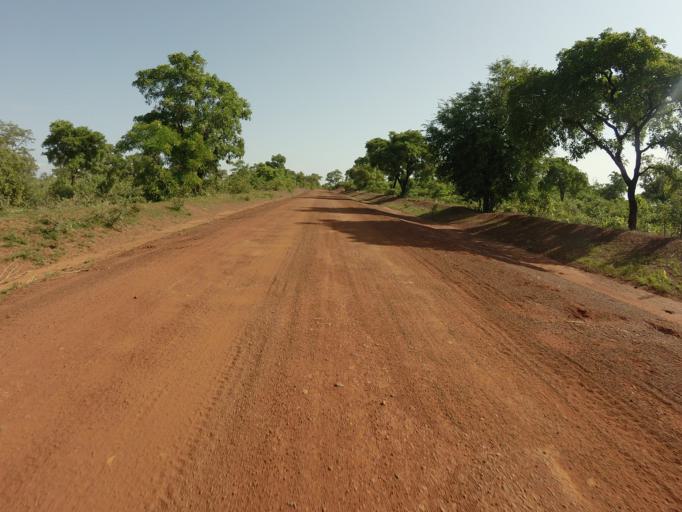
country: GH
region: Upper East
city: Bawku
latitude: 10.7376
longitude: -0.2015
